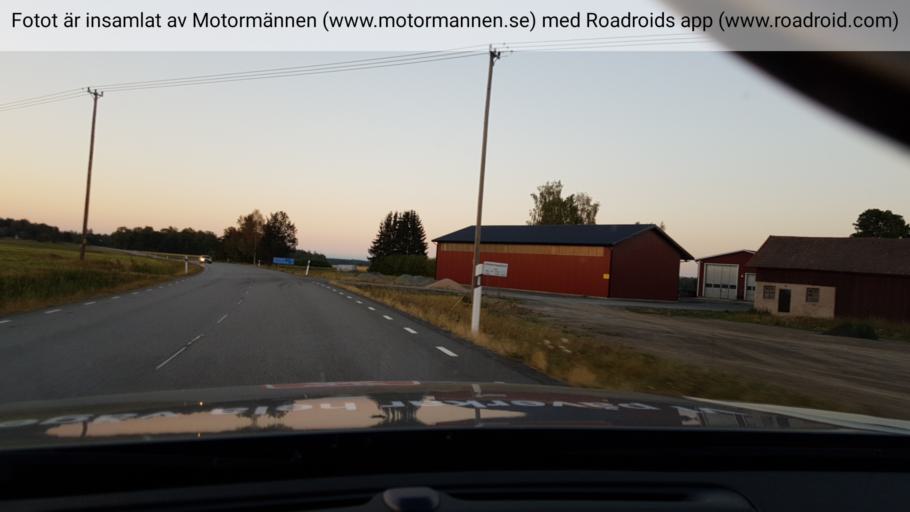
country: SE
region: Uppsala
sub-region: Heby Kommun
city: OEstervala
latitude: 60.1139
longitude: 17.2148
